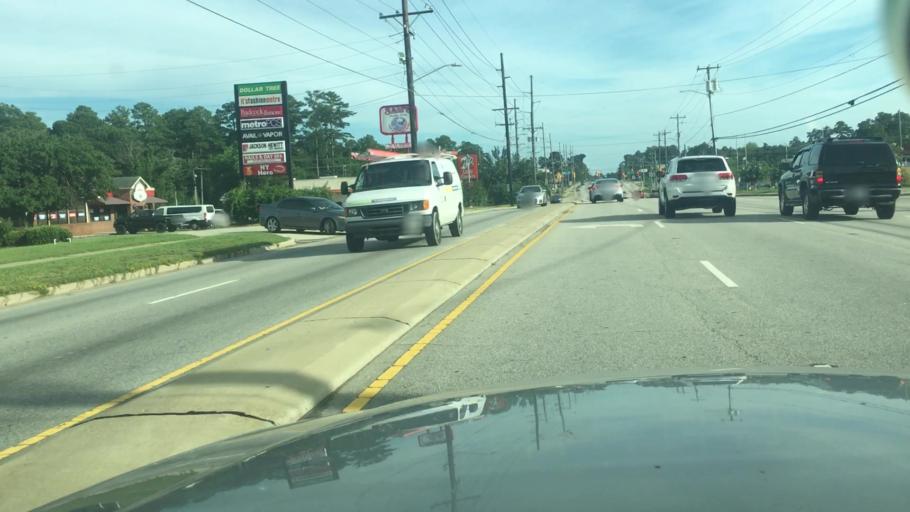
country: US
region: North Carolina
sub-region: Cumberland County
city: Fayetteville
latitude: 35.1095
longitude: -78.8791
